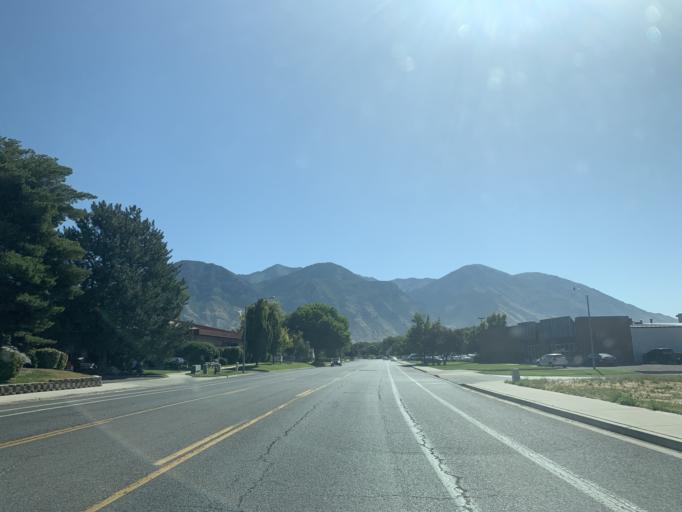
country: US
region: Utah
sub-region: Utah County
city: Provo
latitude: 40.2452
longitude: -111.6870
